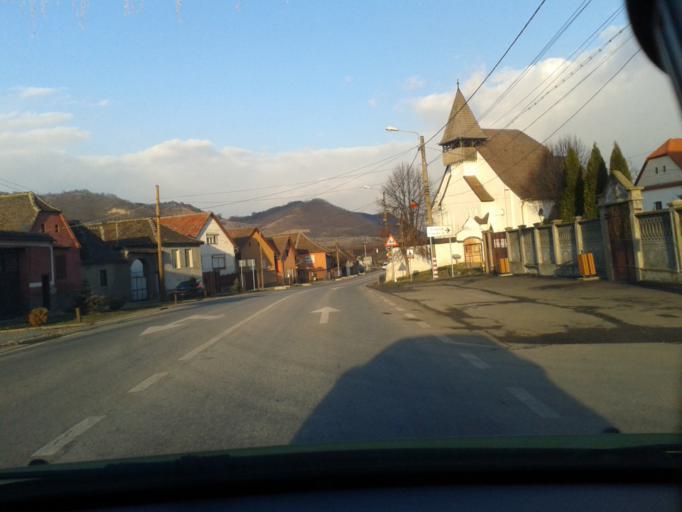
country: RO
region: Sibiu
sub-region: Comuna Copsa Mica
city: Copsa Mica
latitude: 46.1159
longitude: 24.2532
